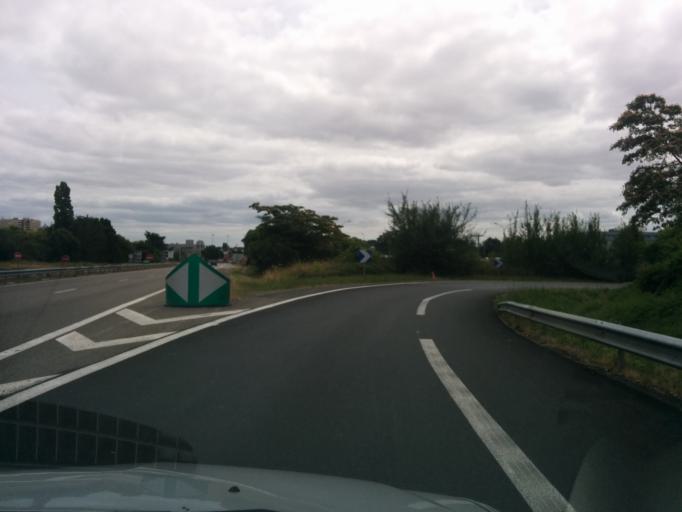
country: FR
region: Pays de la Loire
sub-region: Departement de la Loire-Atlantique
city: Orvault
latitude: 47.2652
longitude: -1.5871
